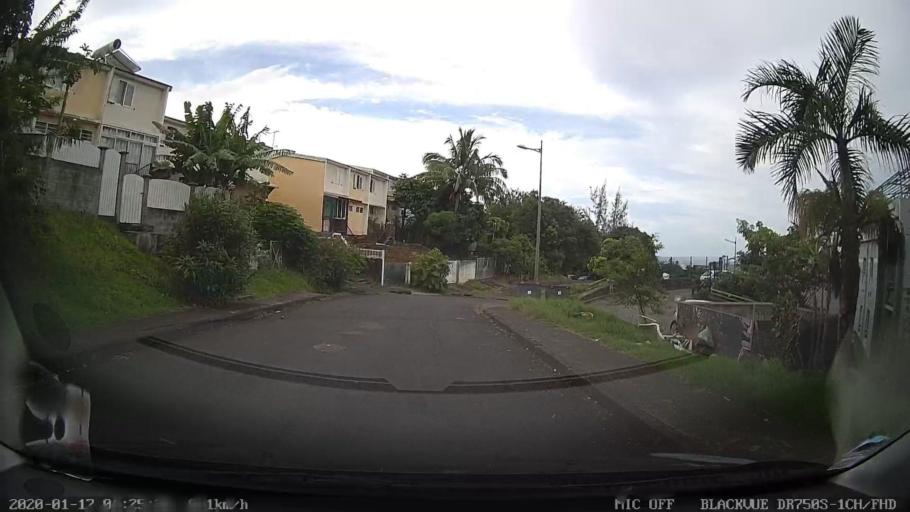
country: RE
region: Reunion
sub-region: Reunion
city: Saint-Denis
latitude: -20.9143
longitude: 55.4869
